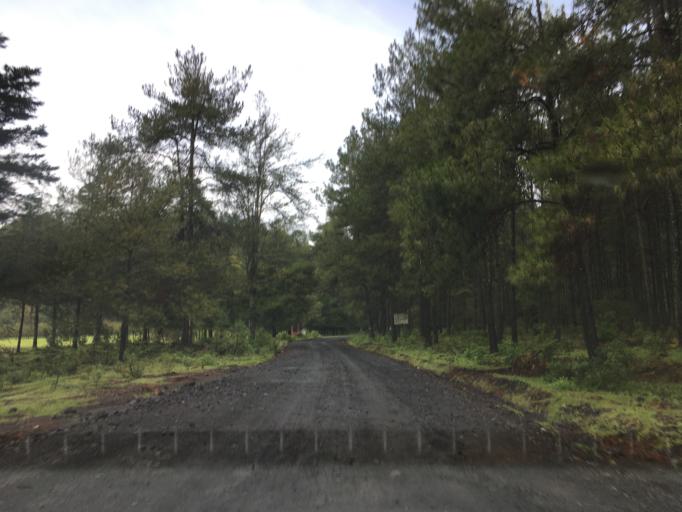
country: MX
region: Michoacan
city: Nuevo San Juan Parangaricutiro
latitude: 19.4586
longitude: -102.1942
